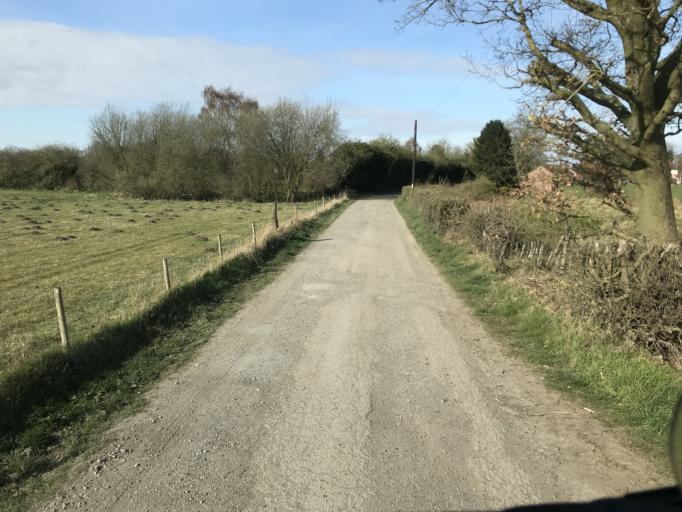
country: GB
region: England
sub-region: Lincolnshire
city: Market Rasen
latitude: 53.3905
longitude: -0.3270
